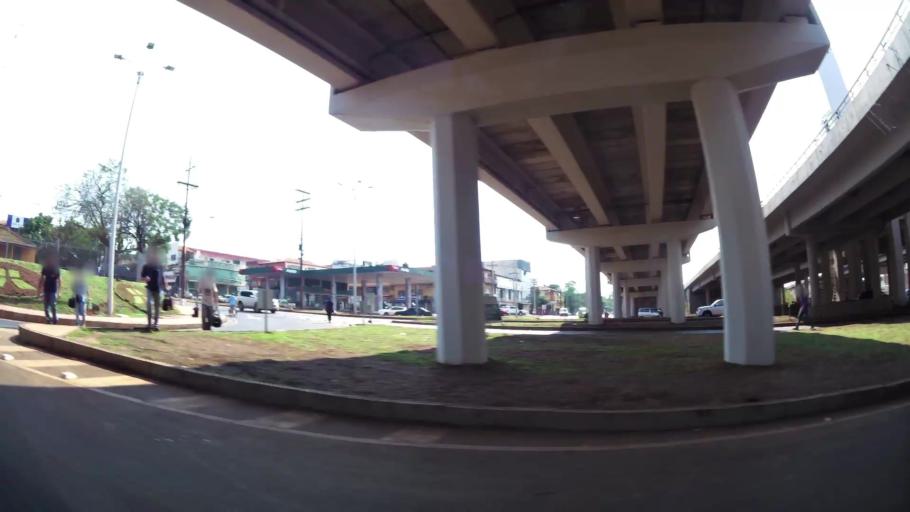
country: PY
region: Alto Parana
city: Ciudad del Este
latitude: -25.5072
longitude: -54.6384
